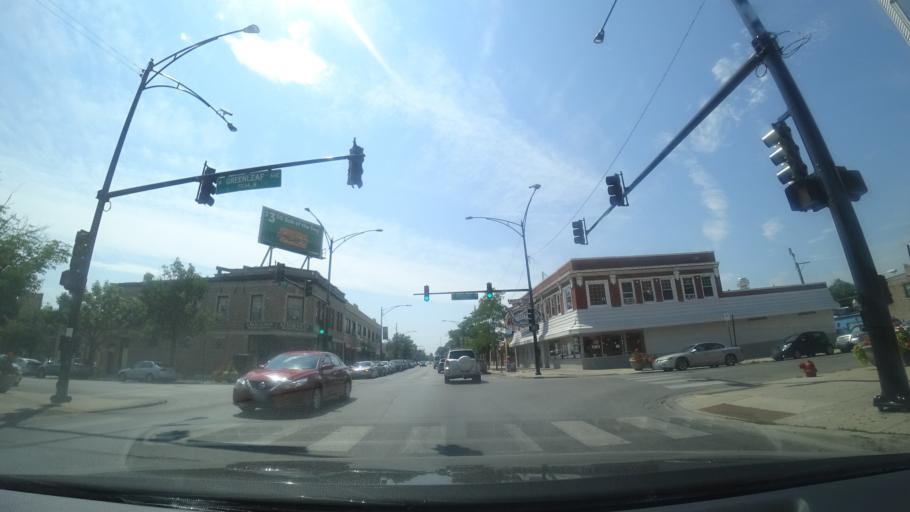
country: US
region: Illinois
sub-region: Cook County
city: Evanston
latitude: 42.0104
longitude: -87.6743
